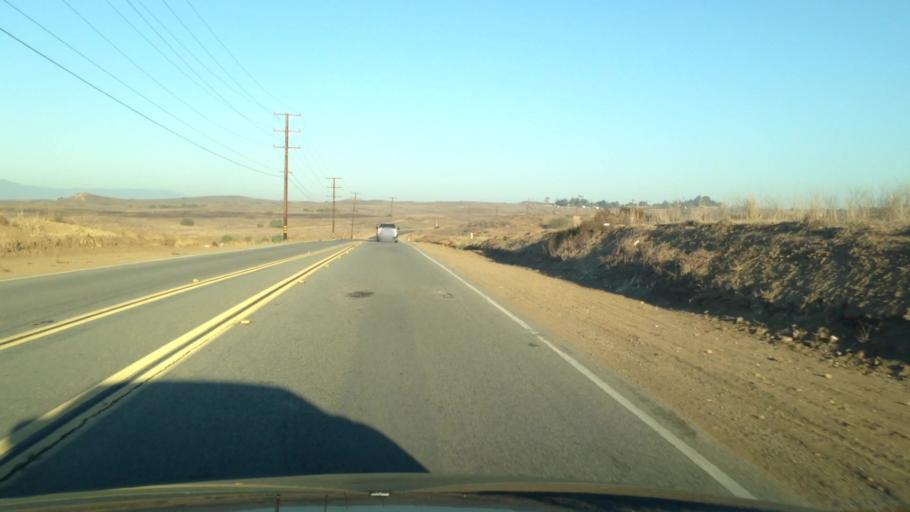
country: US
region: California
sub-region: Riverside County
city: Woodcrest
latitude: 33.8465
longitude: -117.3775
